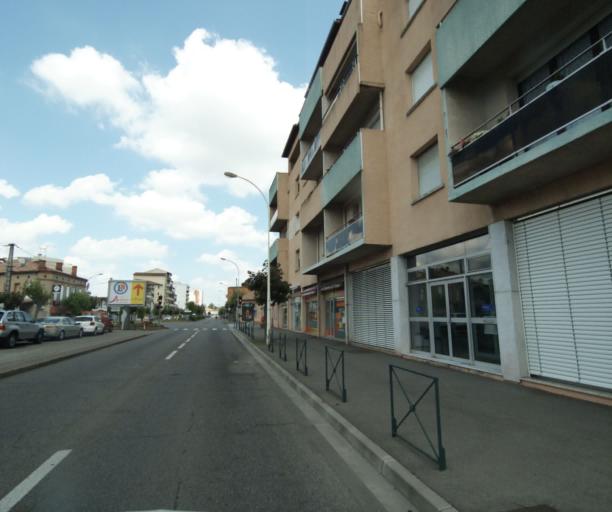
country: FR
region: Midi-Pyrenees
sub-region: Departement du Tarn-et-Garonne
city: Montauban
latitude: 44.0178
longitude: 1.3635
